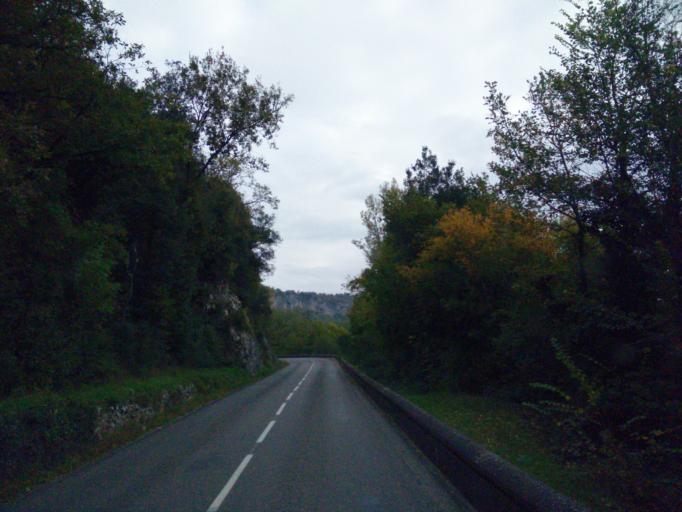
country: FR
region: Midi-Pyrenees
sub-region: Departement du Lot
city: Lalbenque
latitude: 44.4706
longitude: 1.5688
